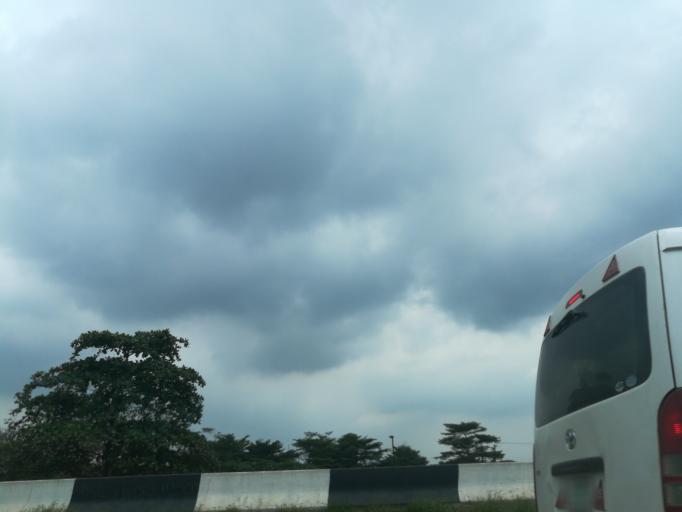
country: NG
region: Lagos
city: Ojota
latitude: 6.6097
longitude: 3.3703
